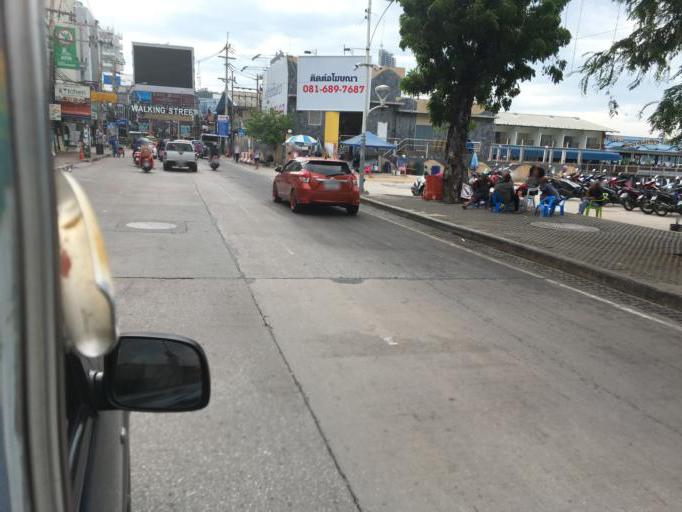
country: TH
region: Chon Buri
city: Phatthaya
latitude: 12.9280
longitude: 100.8754
